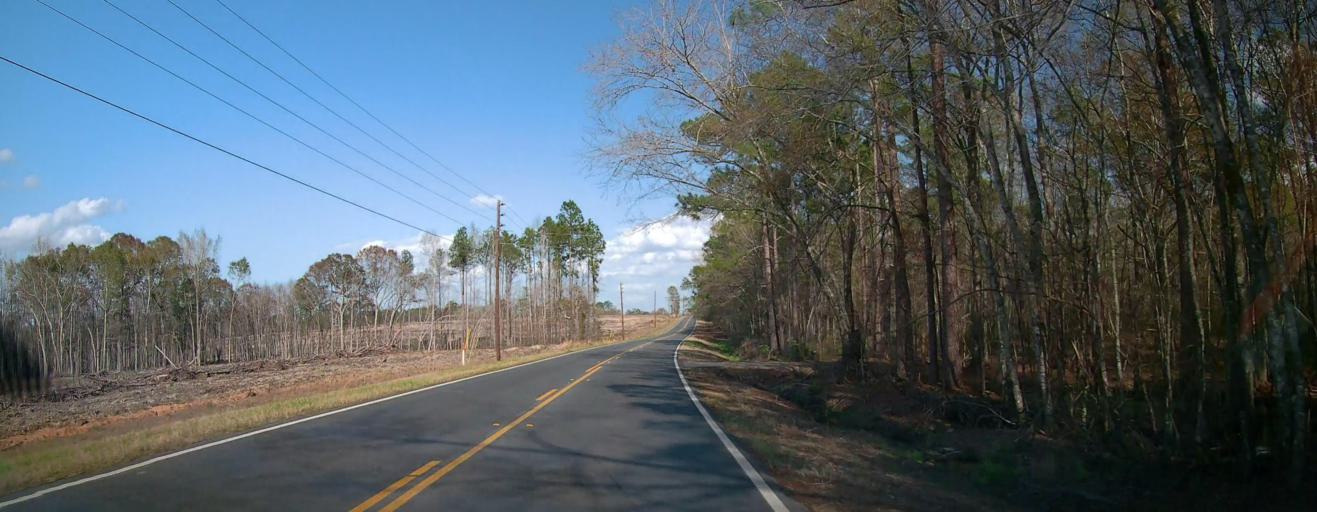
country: US
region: Georgia
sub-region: Telfair County
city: McRae
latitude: 32.0431
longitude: -82.8288
